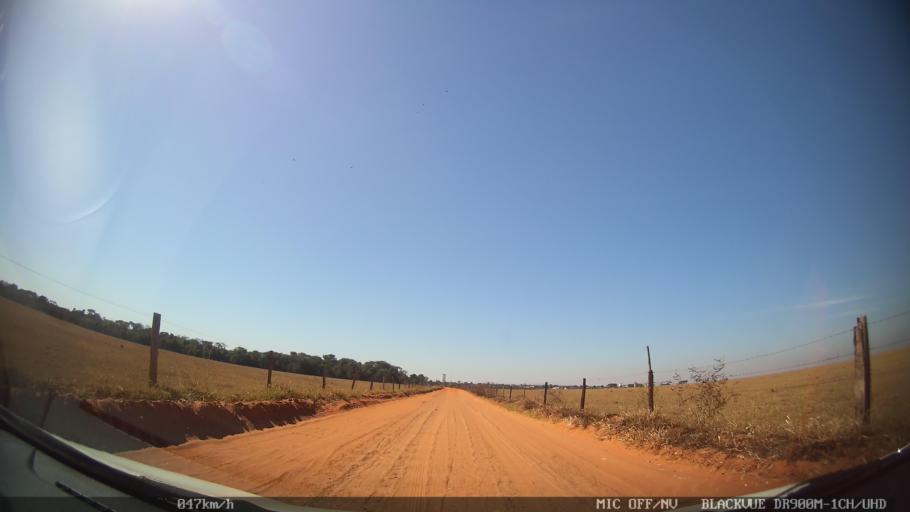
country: BR
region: Sao Paulo
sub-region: Sao Jose Do Rio Preto
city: Sao Jose do Rio Preto
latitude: -20.7417
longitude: -49.4254
